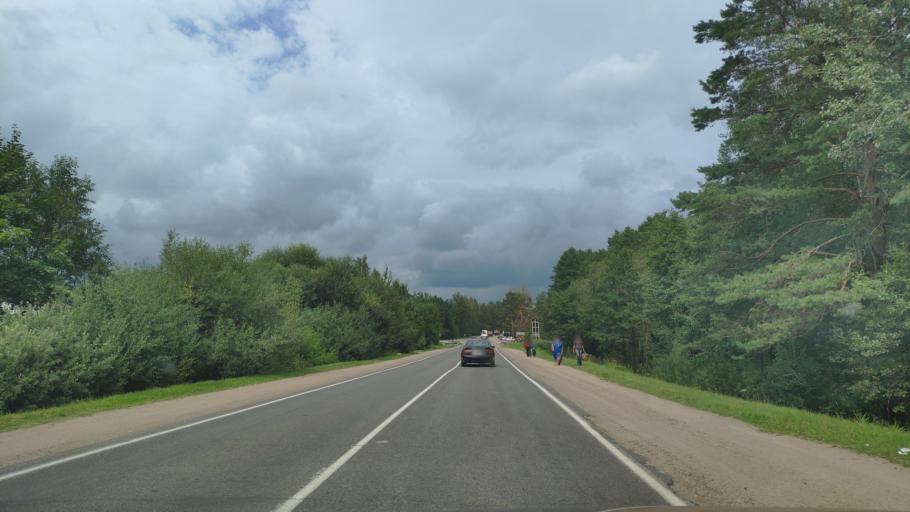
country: BY
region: Minsk
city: Zaslawye
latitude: 53.9840
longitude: 27.2556
